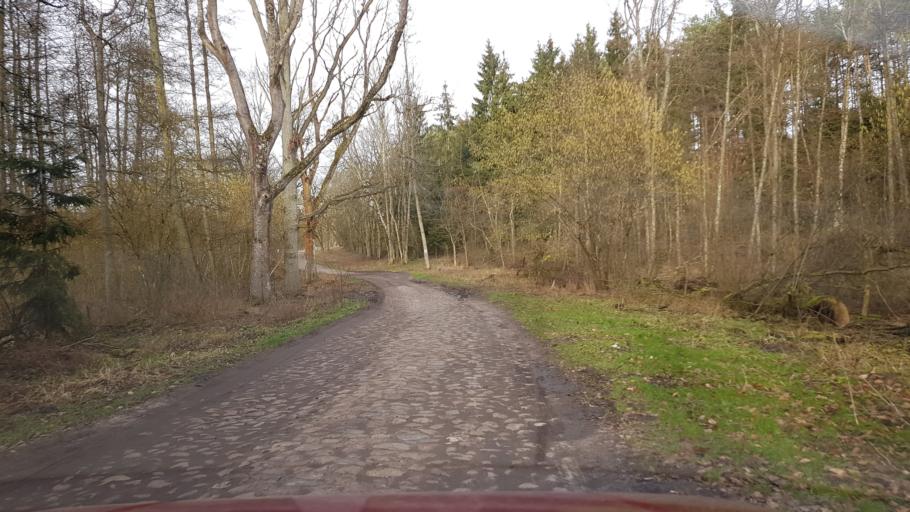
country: PL
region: Lubusz
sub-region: Powiat strzelecko-drezdenecki
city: Strzelce Krajenskie
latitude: 52.9206
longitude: 15.4164
